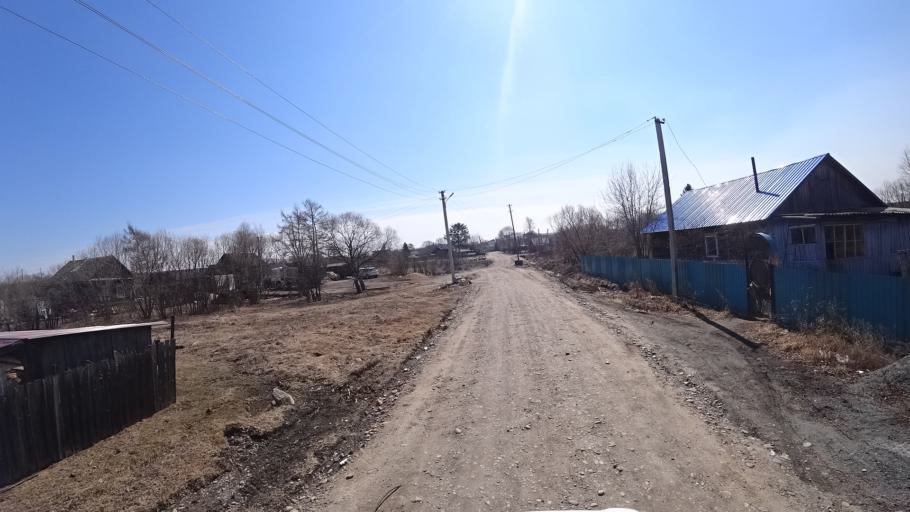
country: RU
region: Amur
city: Novobureyskiy
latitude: 49.7887
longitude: 129.8542
